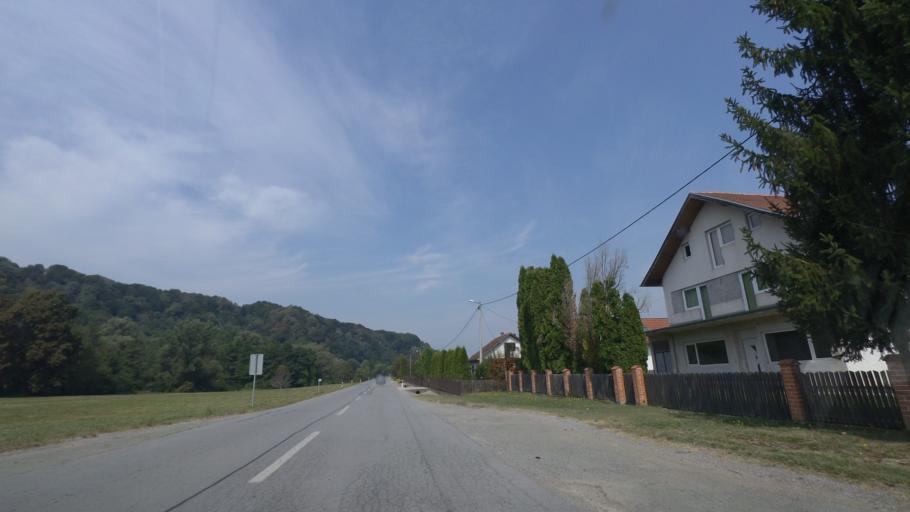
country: HR
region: Sisacko-Moslavacka
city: Glina
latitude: 45.3100
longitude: 16.1162
